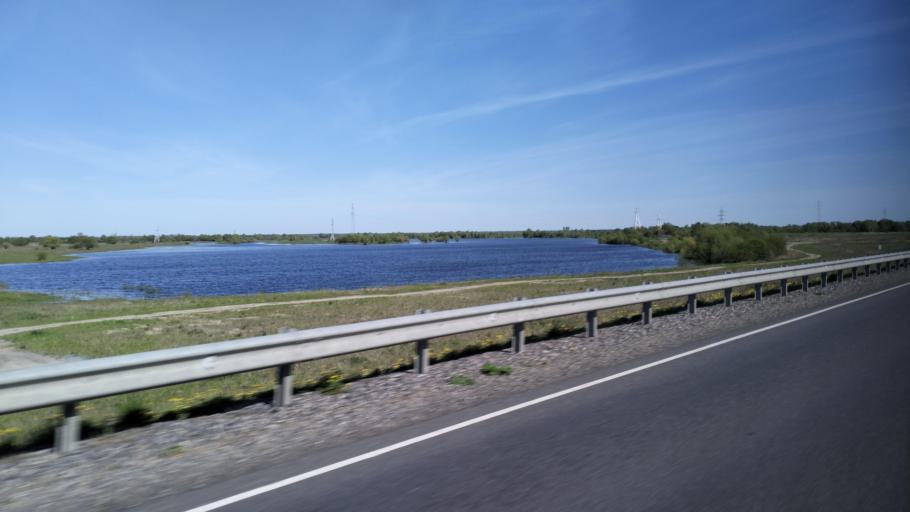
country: BY
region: Gomel
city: Turaw
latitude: 52.0688
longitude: 27.8238
